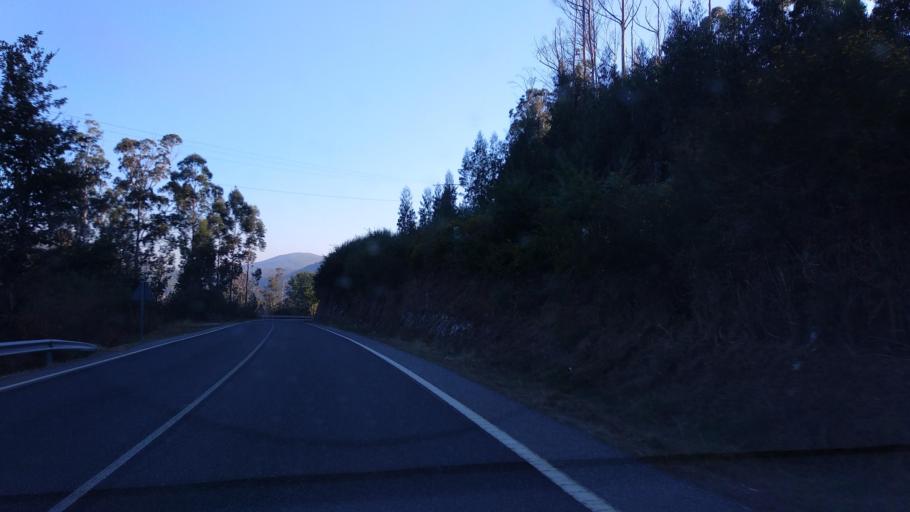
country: ES
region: Galicia
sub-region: Provincia de Pontevedra
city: Ponte Caldelas
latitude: 42.3587
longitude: -8.5414
